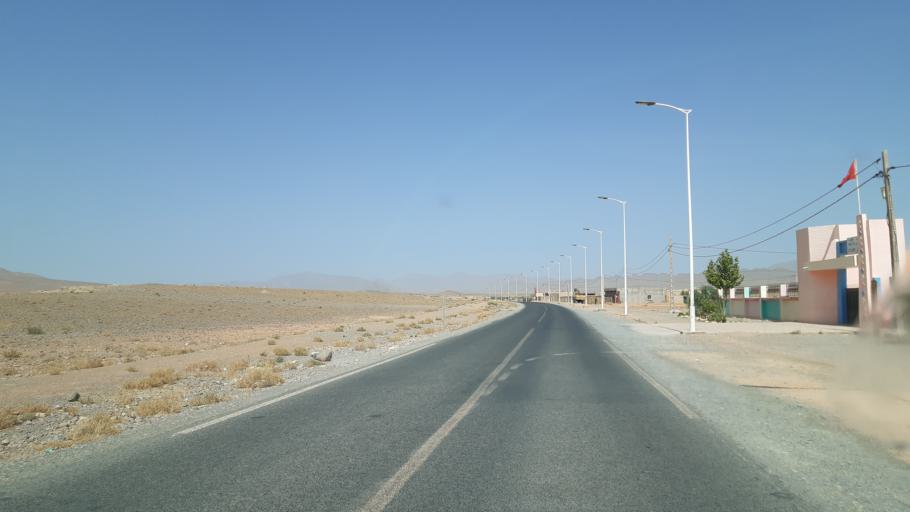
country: MA
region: Meknes-Tafilalet
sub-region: Errachidia
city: Amouguer
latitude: 32.2223
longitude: -4.6798
